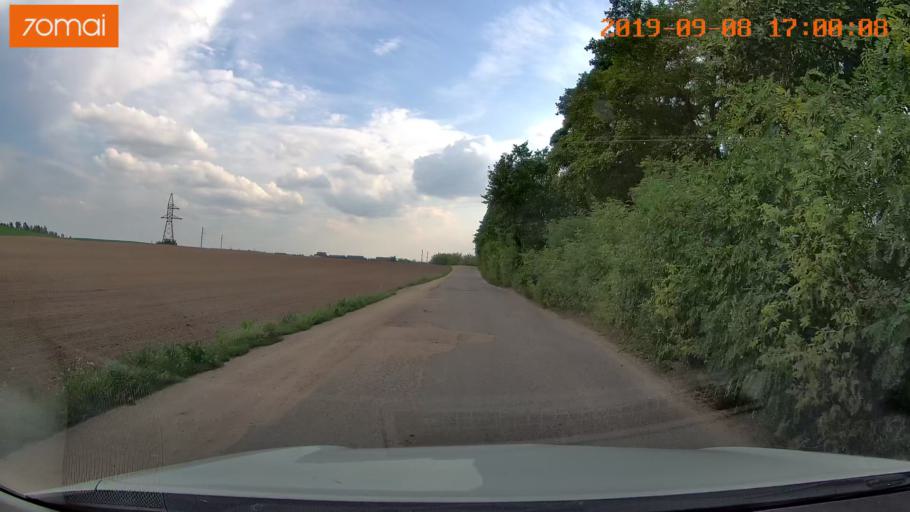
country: BY
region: Grodnenskaya
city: Hrodna
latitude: 53.7178
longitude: 23.9328
